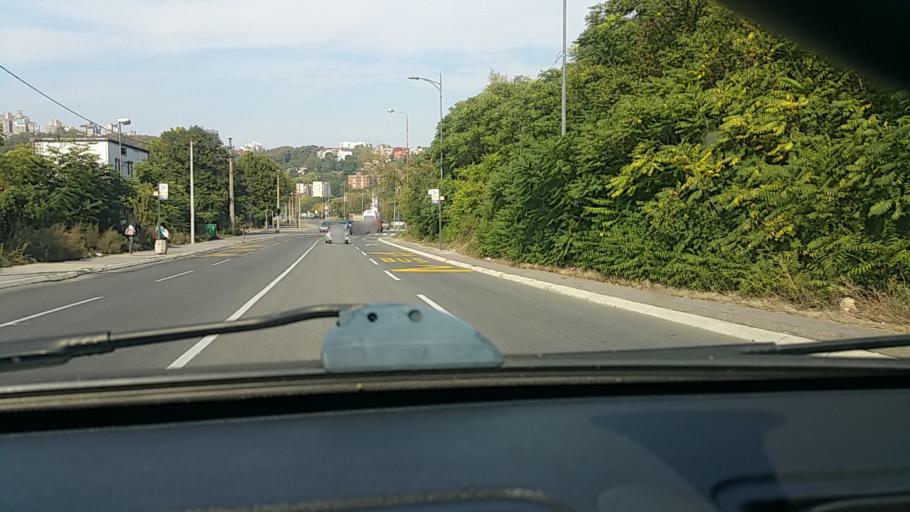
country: RS
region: Central Serbia
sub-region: Belgrade
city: Rakovica
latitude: 44.7378
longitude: 20.4392
